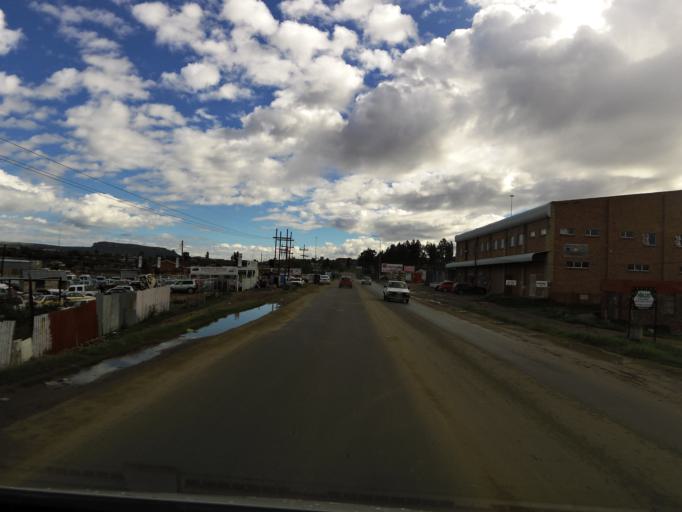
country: LS
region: Maseru
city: Maseru
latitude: -29.3022
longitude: 27.5165
